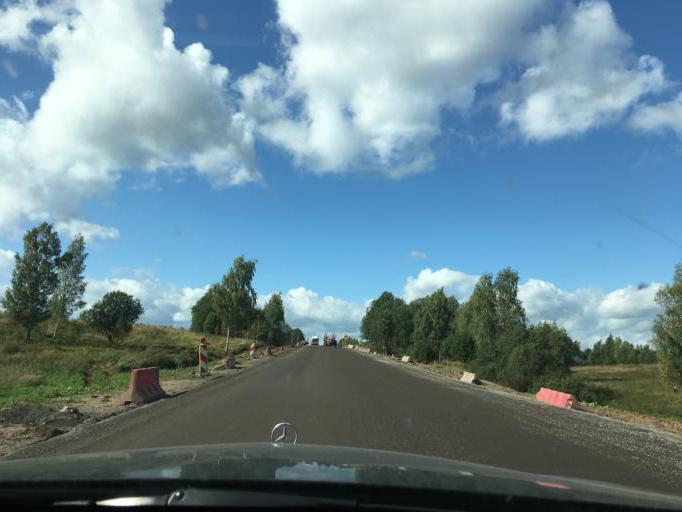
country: RU
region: Pskov
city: Velikiye Luki
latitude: 56.2705
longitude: 30.3732
